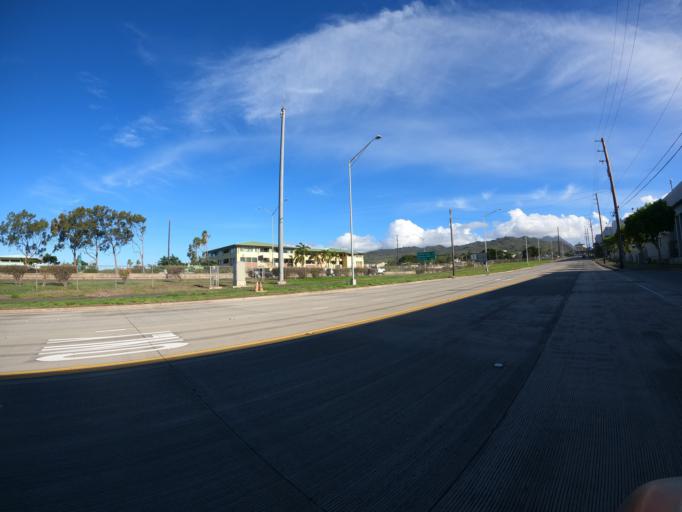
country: US
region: Hawaii
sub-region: Honolulu County
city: Honolulu
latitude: 21.3363
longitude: -157.8860
